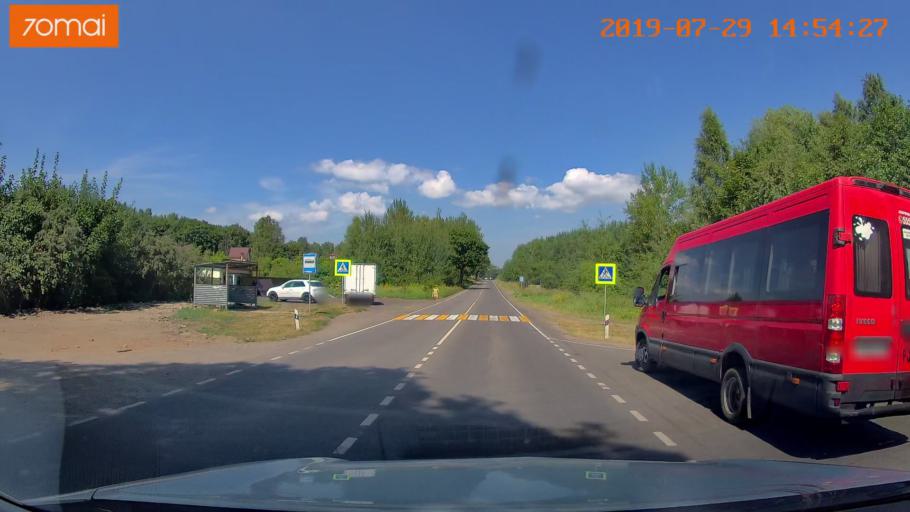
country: RU
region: Kaliningrad
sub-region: Gorod Kaliningrad
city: Baltiysk
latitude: 54.6741
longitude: 19.9248
